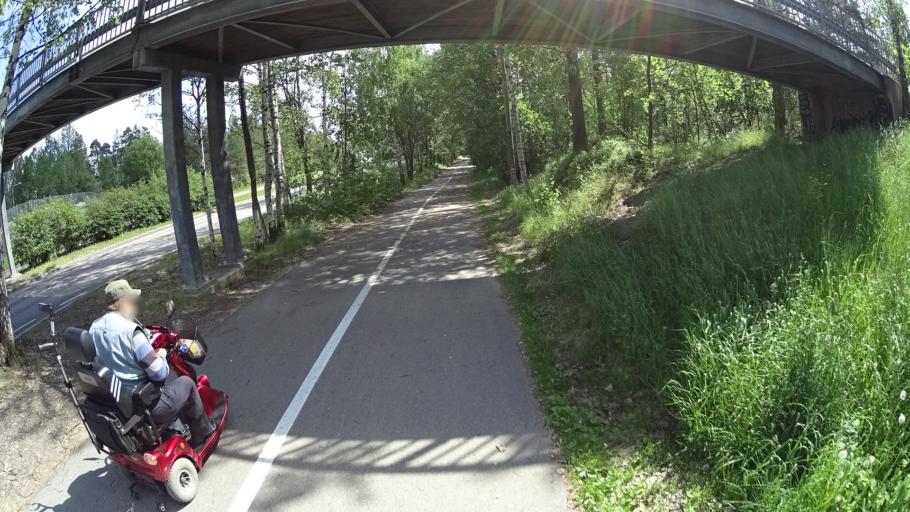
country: FI
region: Uusimaa
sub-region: Helsinki
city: Vantaa
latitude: 60.2369
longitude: 25.0997
